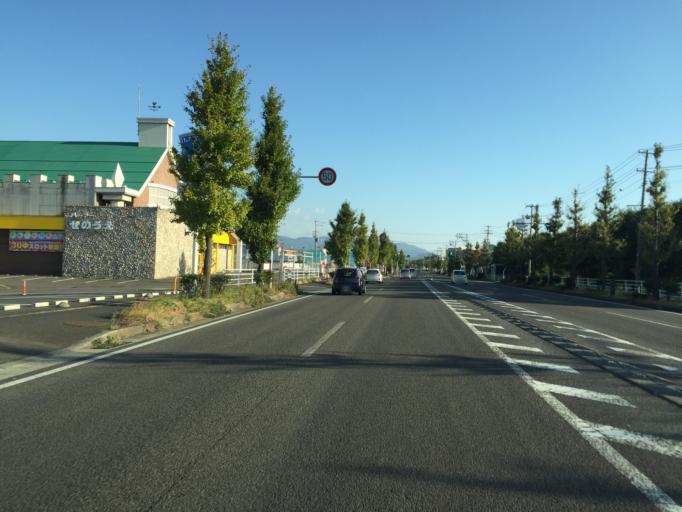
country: JP
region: Fukushima
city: Hobaramachi
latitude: 37.8107
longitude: 140.4980
